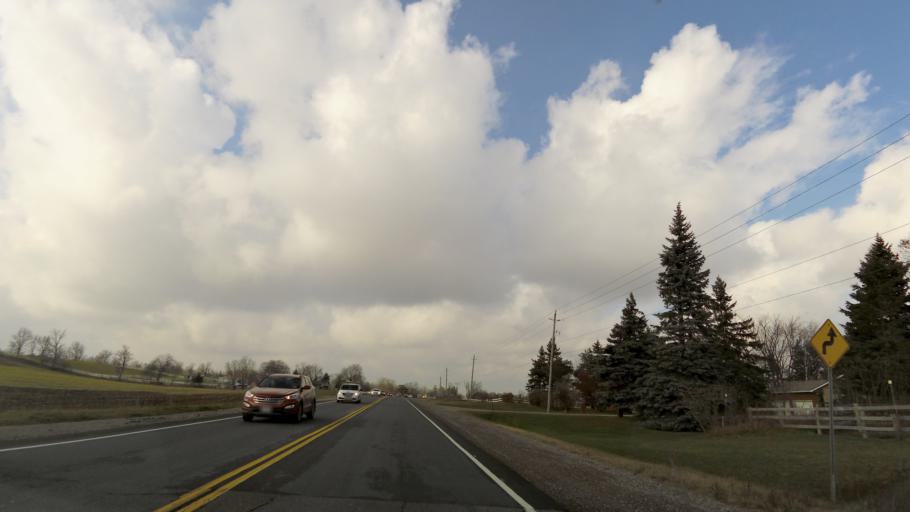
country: CA
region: Ontario
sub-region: Wellington County
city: Guelph
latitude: 43.4372
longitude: -80.1032
